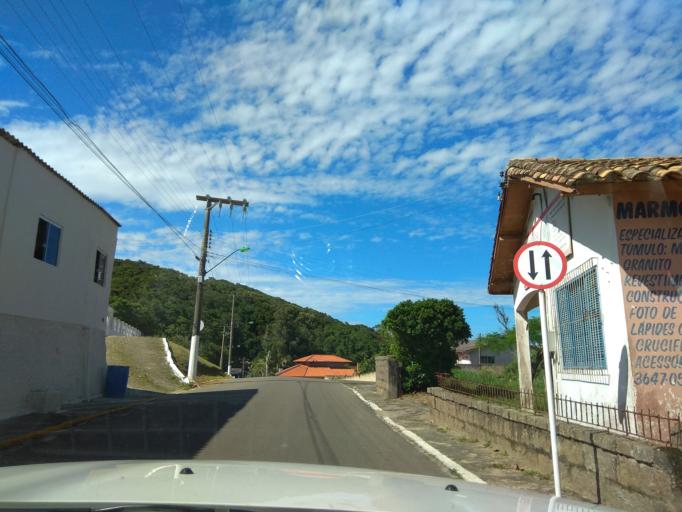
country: BR
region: Santa Catarina
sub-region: Laguna
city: Laguna
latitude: -28.4822
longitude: -48.7755
